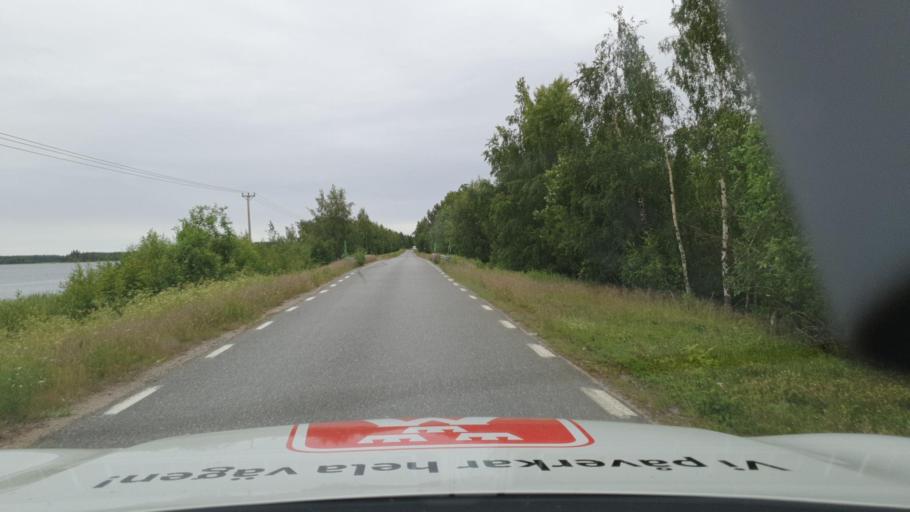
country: SE
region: Vaesterbotten
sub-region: Nordmalings Kommun
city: Nordmaling
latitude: 63.4683
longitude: 19.4638
